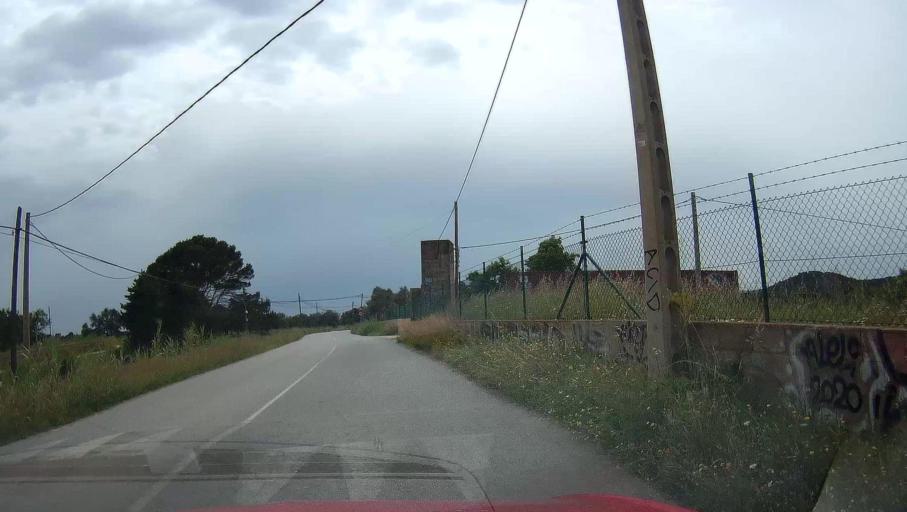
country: ES
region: Balearic Islands
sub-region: Illes Balears
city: Ibiza
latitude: 38.8771
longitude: 1.3569
